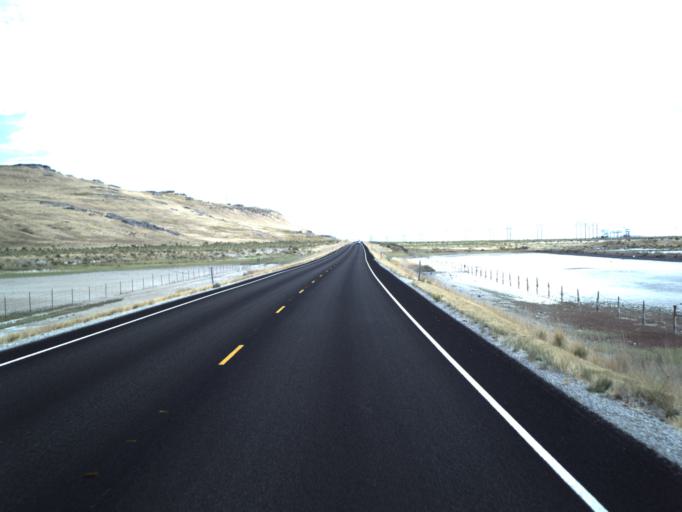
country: US
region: Utah
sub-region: Box Elder County
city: Tremonton
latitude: 41.6243
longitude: -112.3926
